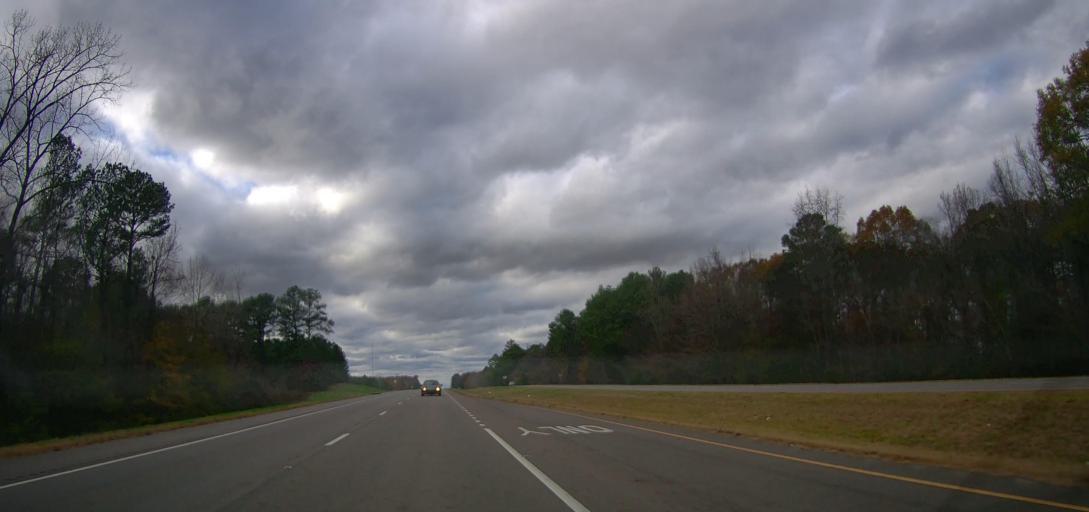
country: US
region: Alabama
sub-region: Morgan County
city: Danville
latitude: 34.3510
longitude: -87.0447
